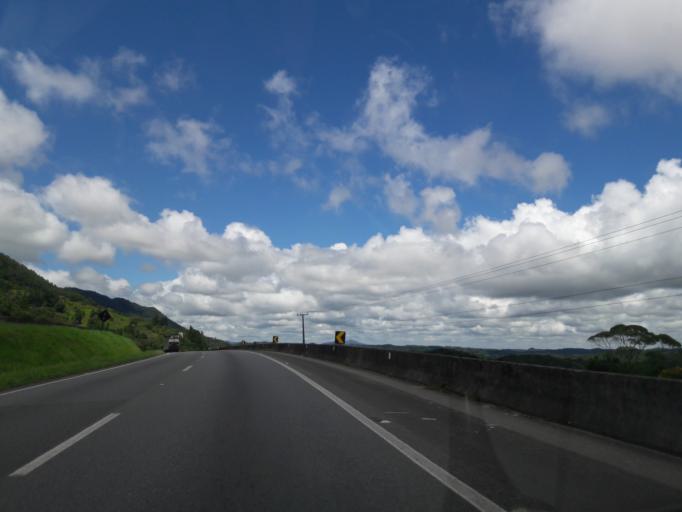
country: BR
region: Parana
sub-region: Campina Grande Do Sul
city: Campina Grande do Sul
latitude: -25.1477
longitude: -48.8591
